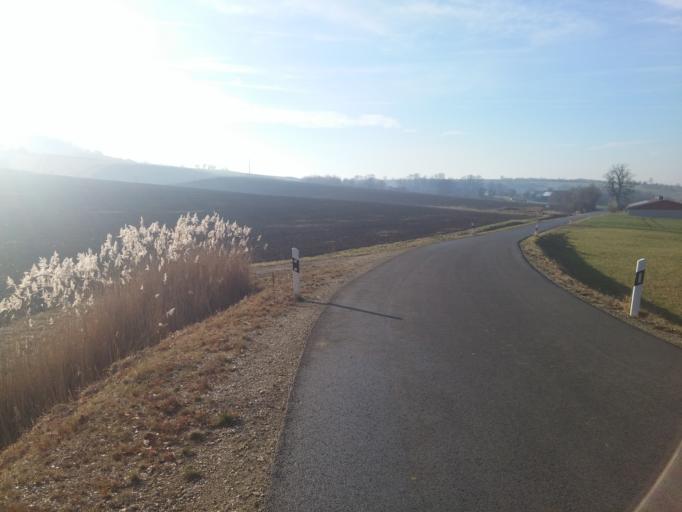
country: DE
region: Bavaria
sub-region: Upper Franconia
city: Untersiemau
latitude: 50.1723
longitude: 10.9722
